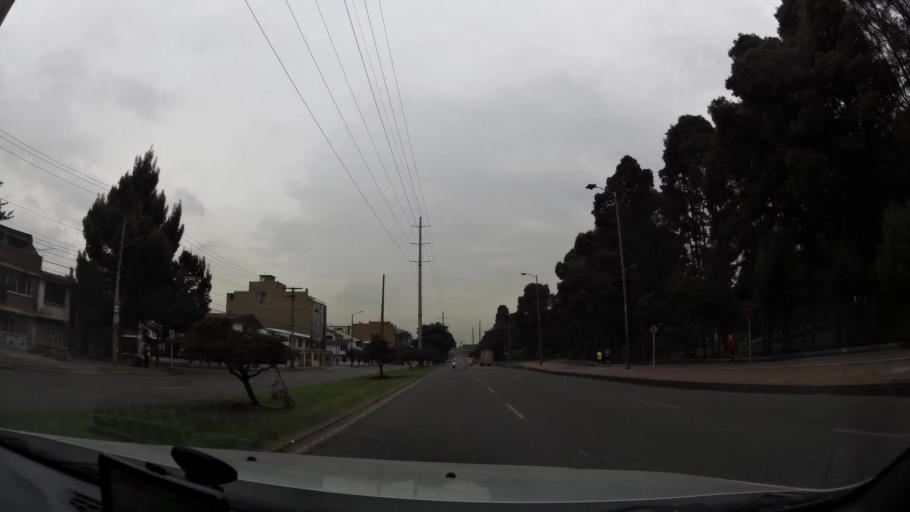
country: CO
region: Bogota D.C.
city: Bogota
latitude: 4.6558
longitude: -74.0985
